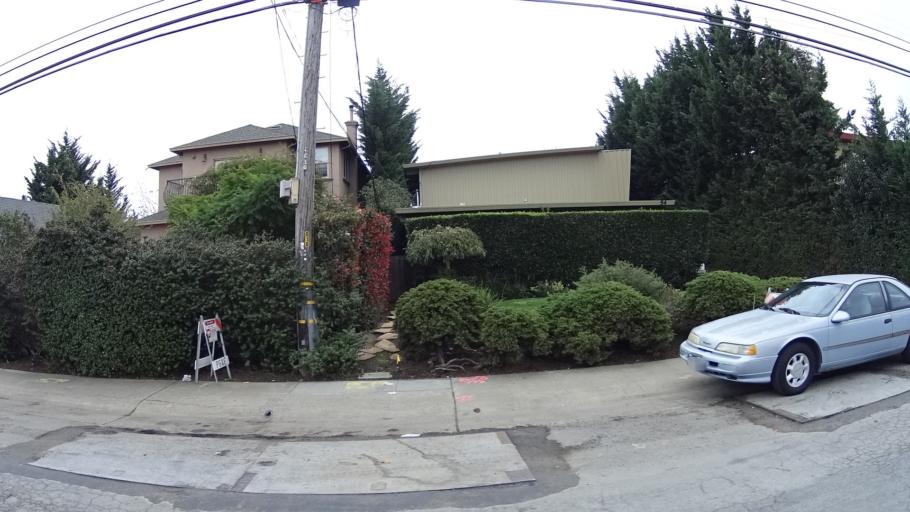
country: US
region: California
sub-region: San Mateo County
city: Belmont
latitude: 37.5342
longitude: -122.2909
